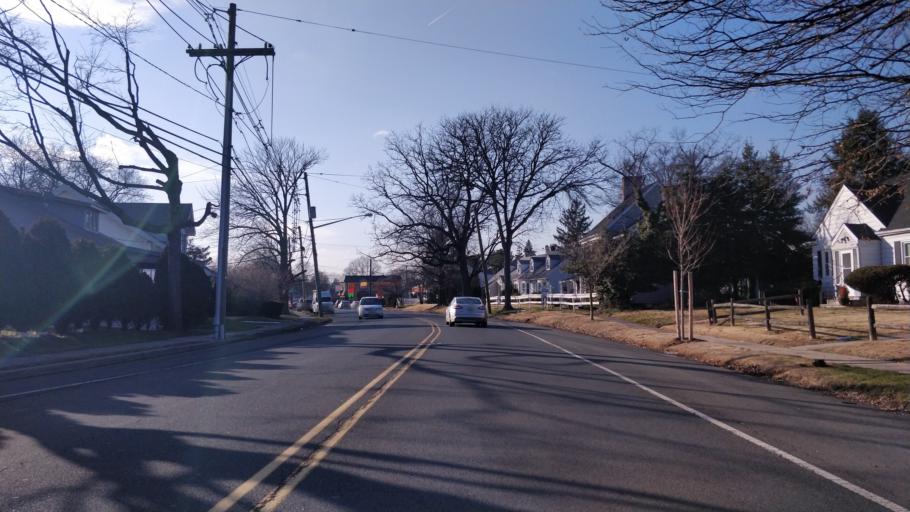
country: US
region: New Jersey
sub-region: Union County
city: Union
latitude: 40.6978
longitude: -74.2593
